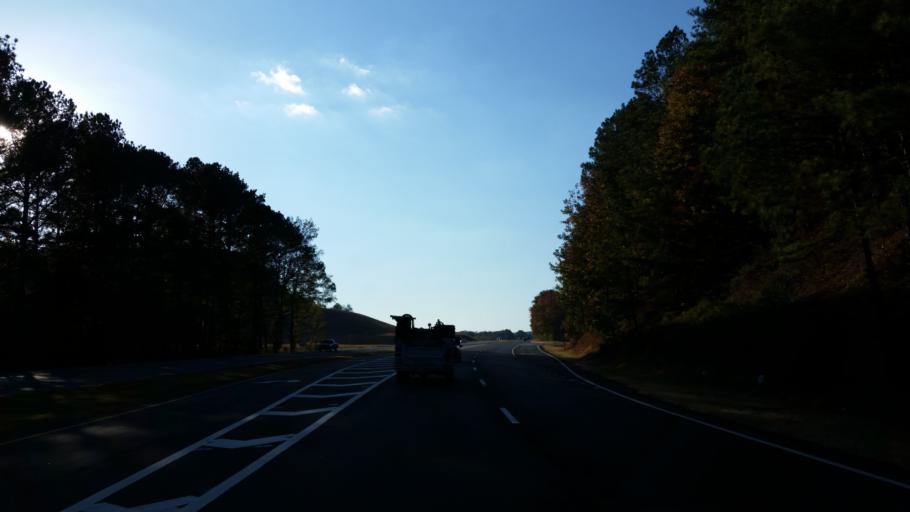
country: US
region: Georgia
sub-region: Bartow County
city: Cartersville
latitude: 34.2173
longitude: -84.8608
